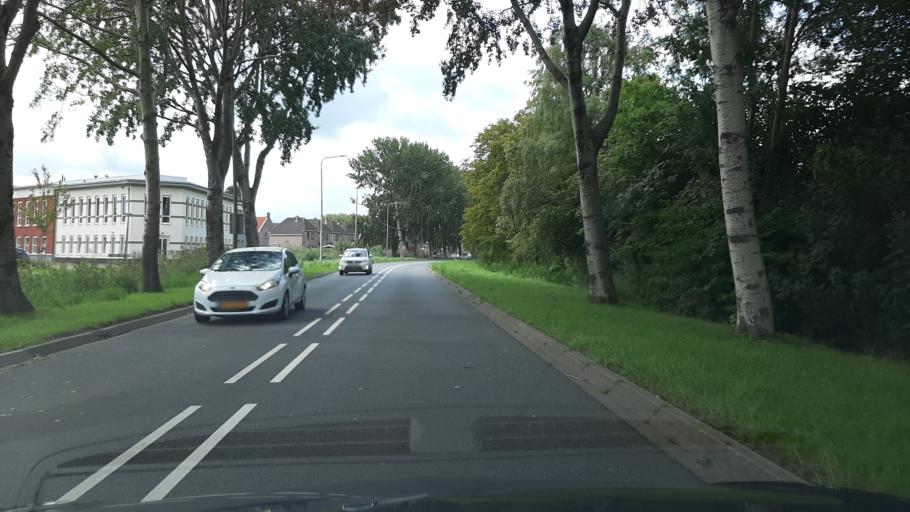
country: NL
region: Overijssel
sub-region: Gemeente Zwartewaterland
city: Hasselt
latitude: 52.6426
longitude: 6.0737
